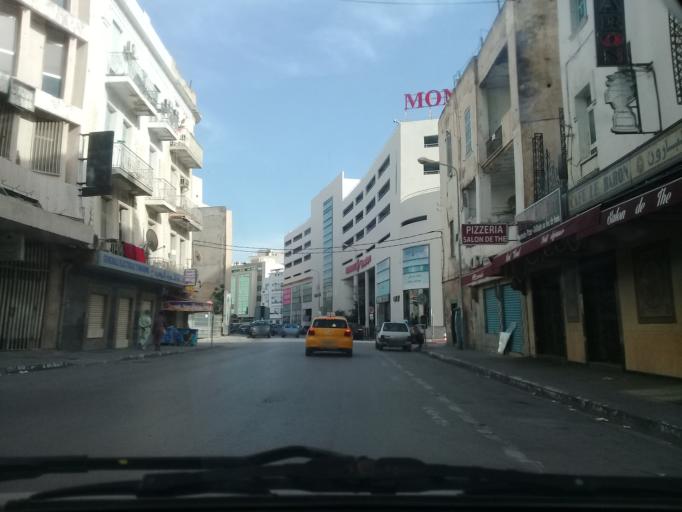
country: TN
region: Tunis
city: Tunis
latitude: 36.8028
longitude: 10.1828
